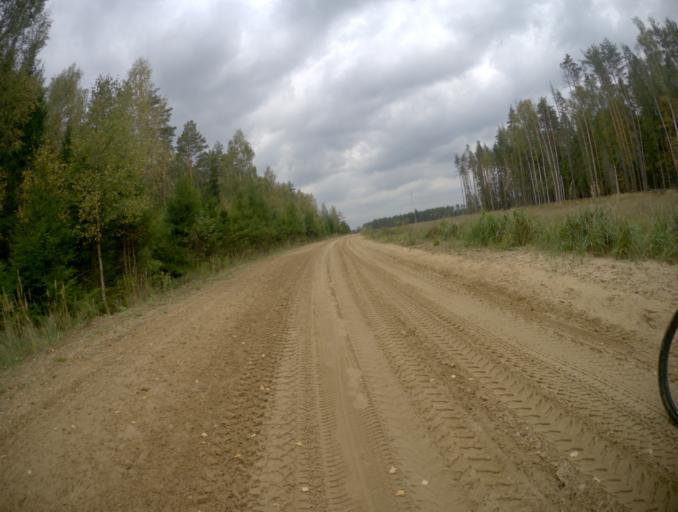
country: RU
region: Vladimir
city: Kideksha
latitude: 56.4712
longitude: 40.6813
